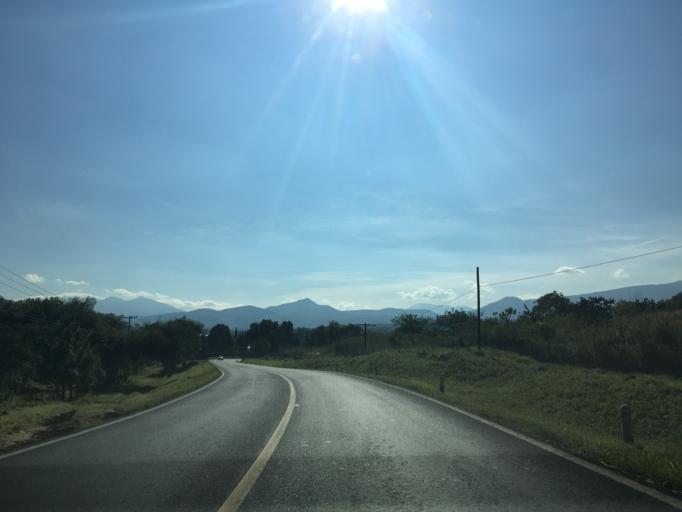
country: MX
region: Mexico
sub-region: Chalco
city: Chilchota
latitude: 19.8564
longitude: -102.1317
